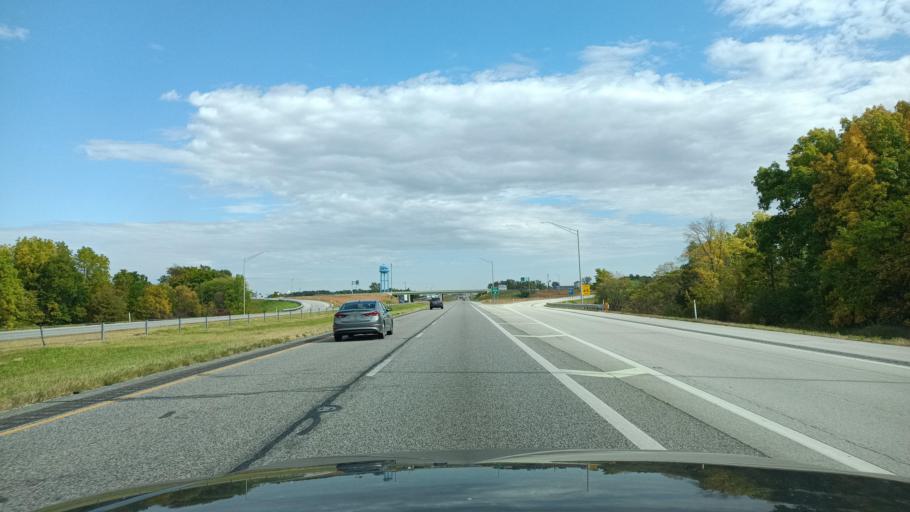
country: US
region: Indiana
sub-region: Huntington County
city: Markle
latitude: 40.8243
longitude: -85.3572
